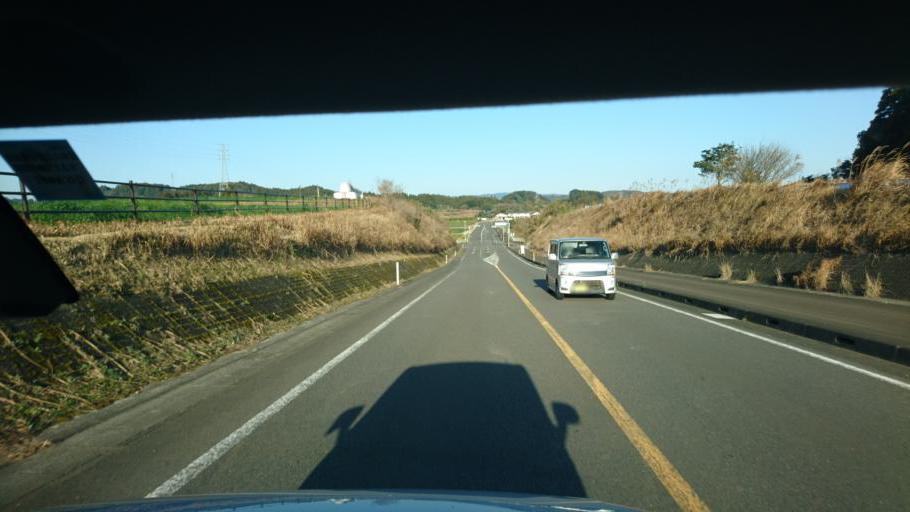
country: JP
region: Miyazaki
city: Miyazaki-shi
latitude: 31.8506
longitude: 131.3791
